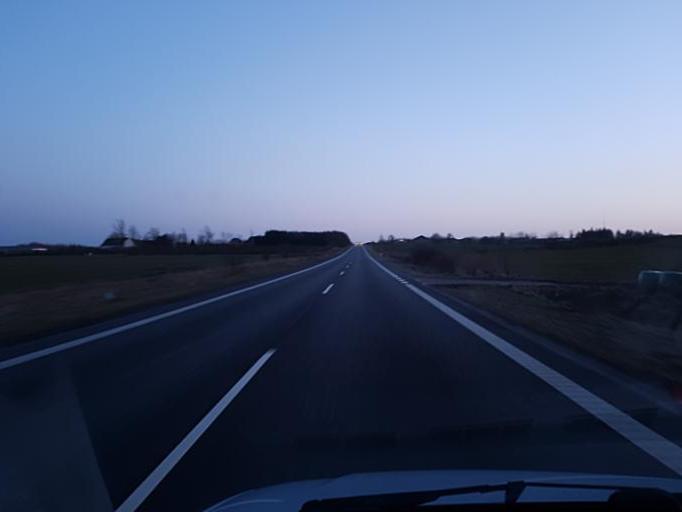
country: DK
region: Central Jutland
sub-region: Ringkobing-Skjern Kommune
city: Videbaek
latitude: 56.2068
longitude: 8.5828
